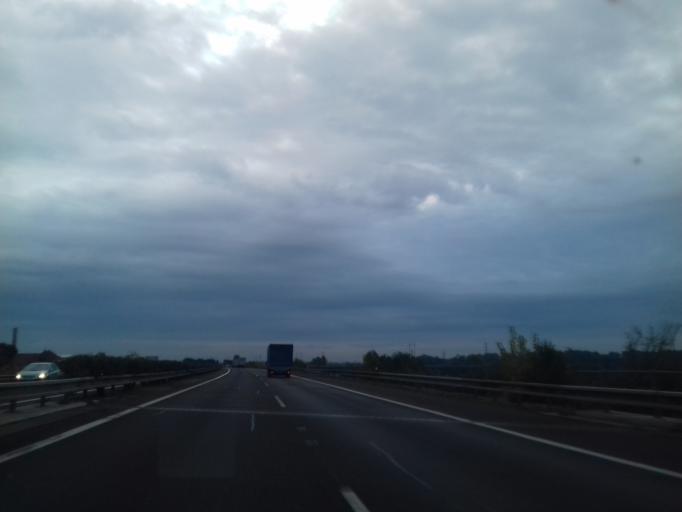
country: CZ
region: Central Bohemia
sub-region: Okres Nymburk
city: Sadska
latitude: 50.1163
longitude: 14.9581
